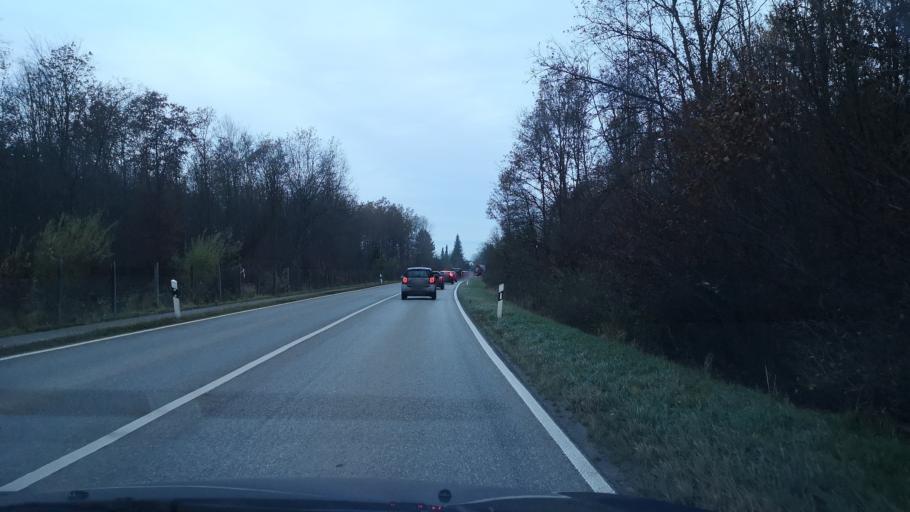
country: DE
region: Bavaria
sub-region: Upper Bavaria
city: Forstinning
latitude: 48.1547
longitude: 11.9062
